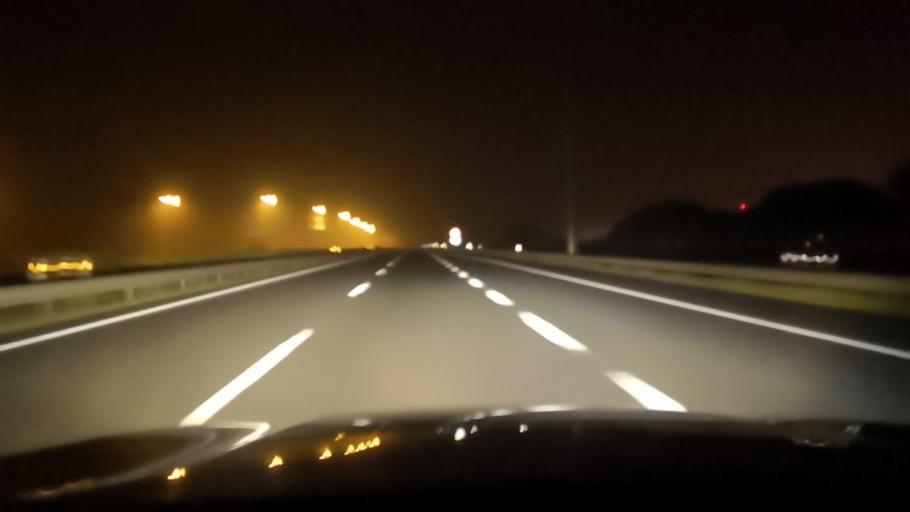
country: PT
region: Santarem
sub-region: Benavente
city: Benavente
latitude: 38.9549
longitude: -8.8277
